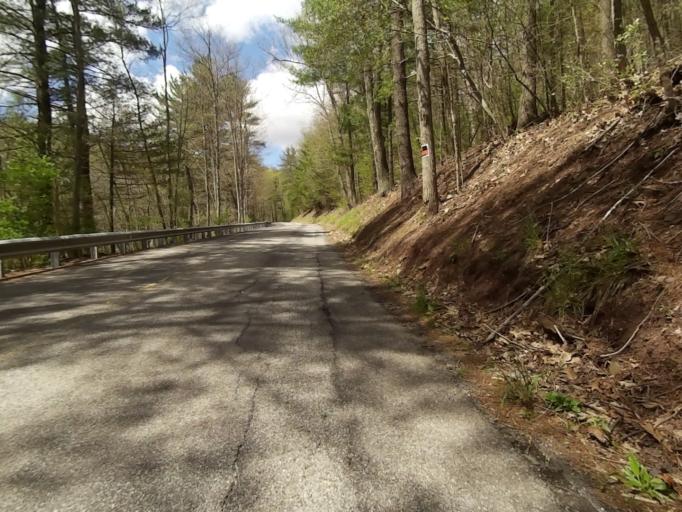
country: US
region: Pennsylvania
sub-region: Centre County
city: Milesburg
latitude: 40.9535
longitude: -77.8899
